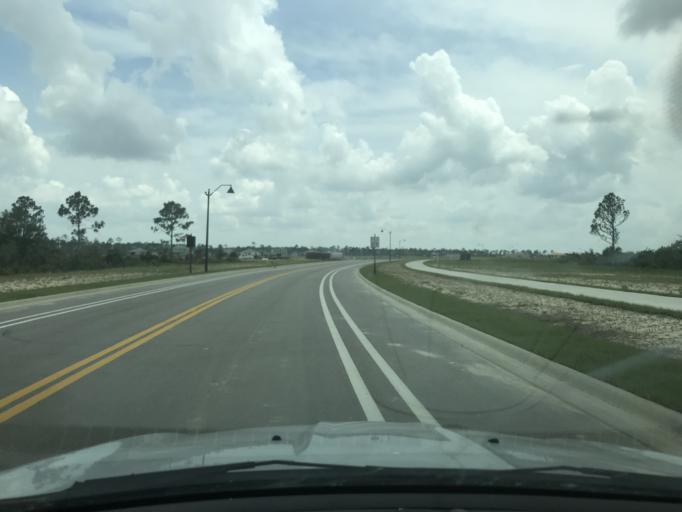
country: US
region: Florida
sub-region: Lee County
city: Olga
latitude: 26.7929
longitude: -81.7346
